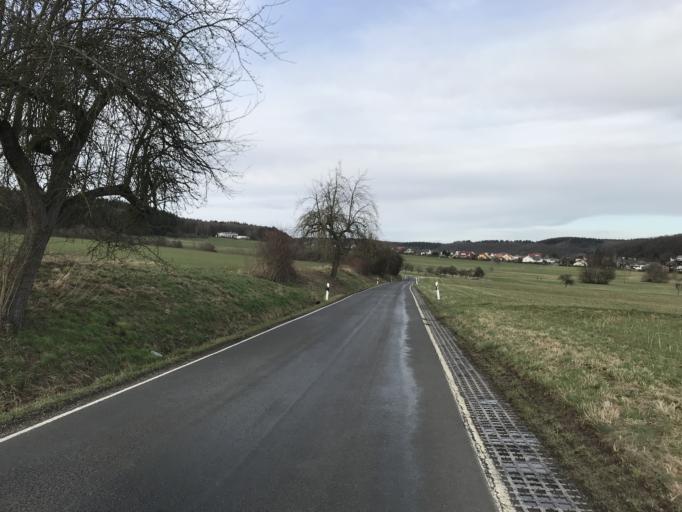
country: DE
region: Hesse
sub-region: Regierungsbezirk Giessen
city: Heuchelheim
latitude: 50.6342
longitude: 8.5855
